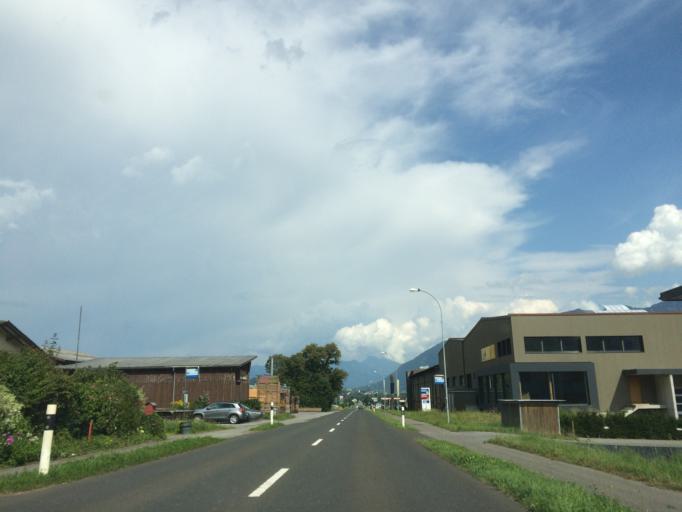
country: CH
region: Saint Gallen
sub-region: Wahlkreis Werdenberg
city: Gams
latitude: 47.2054
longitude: 9.4534
